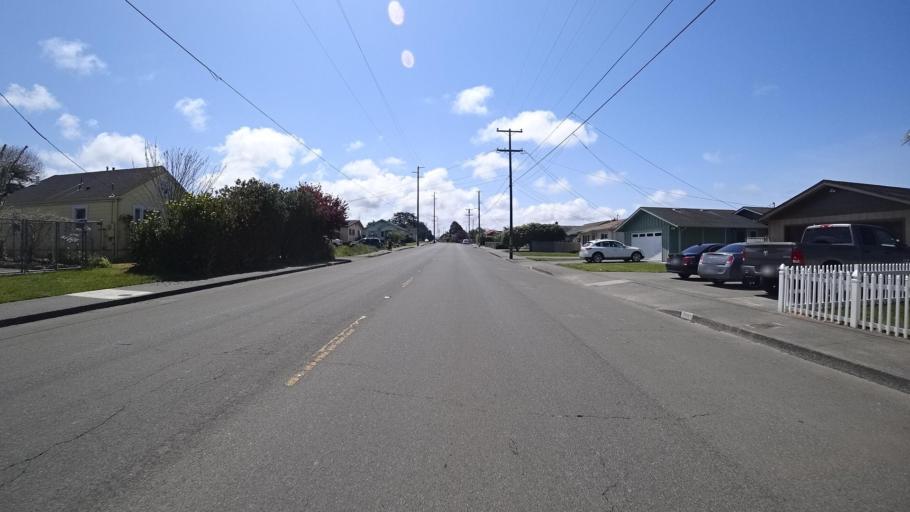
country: US
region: California
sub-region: Humboldt County
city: Bayview
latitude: 40.7791
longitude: -124.1803
